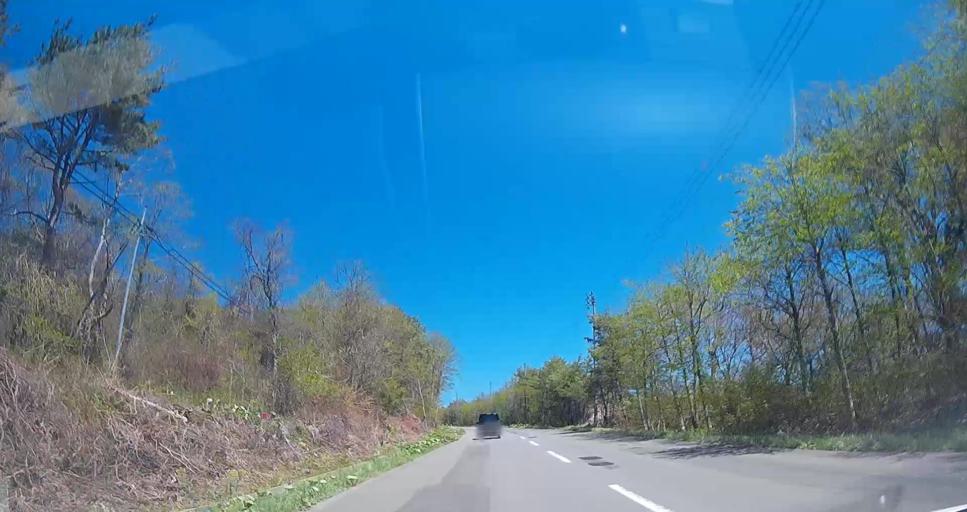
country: JP
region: Aomori
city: Mutsu
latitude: 41.2782
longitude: 141.3931
